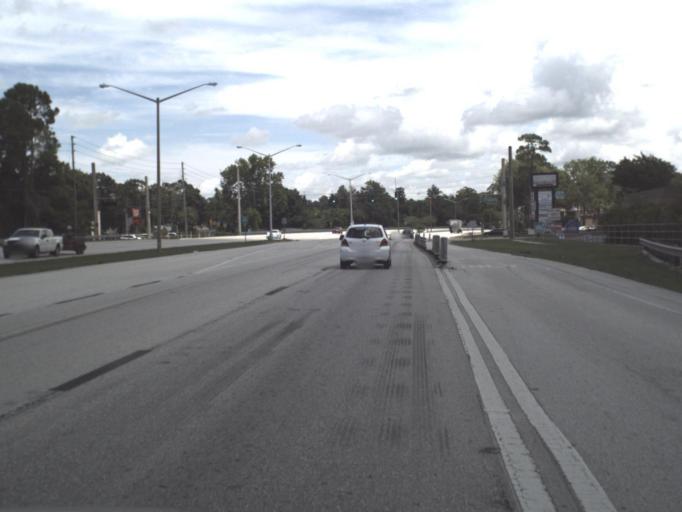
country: US
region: Florida
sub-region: Pinellas County
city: East Lake
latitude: 28.0881
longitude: -82.6991
